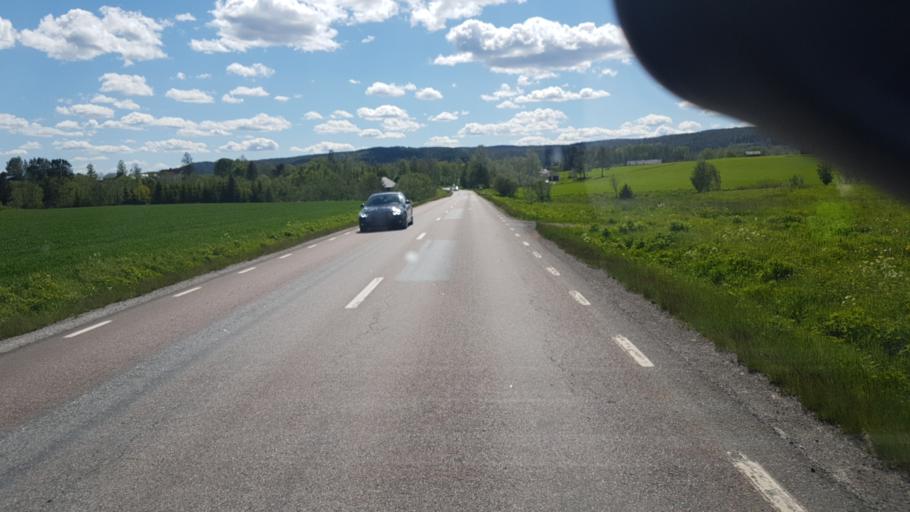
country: SE
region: Vaermland
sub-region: Sunne Kommun
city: Sunne
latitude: 59.7274
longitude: 13.1217
